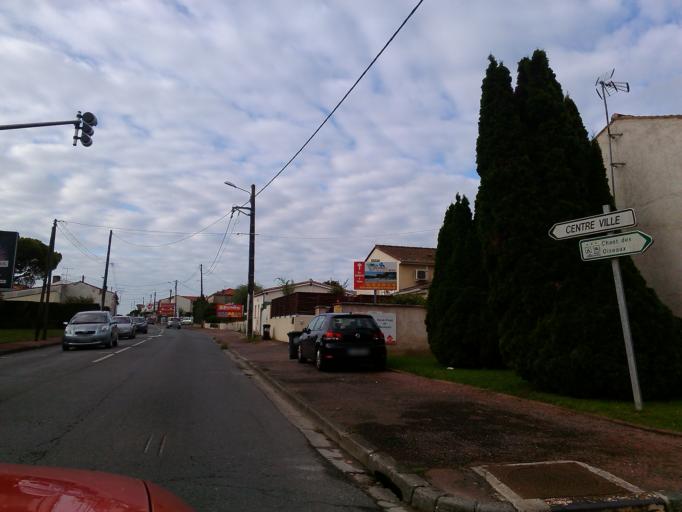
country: FR
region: Poitou-Charentes
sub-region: Departement de la Charente-Maritime
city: Royan
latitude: 45.6447
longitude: -1.0248
